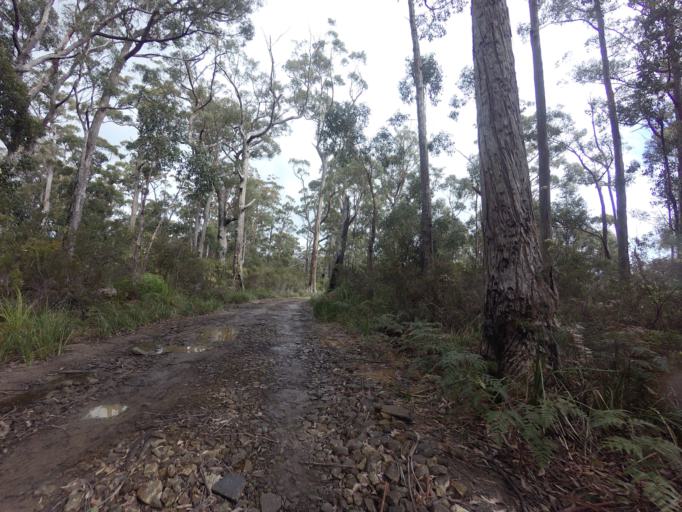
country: AU
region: Tasmania
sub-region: Huon Valley
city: Geeveston
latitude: -43.4643
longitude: 146.9251
